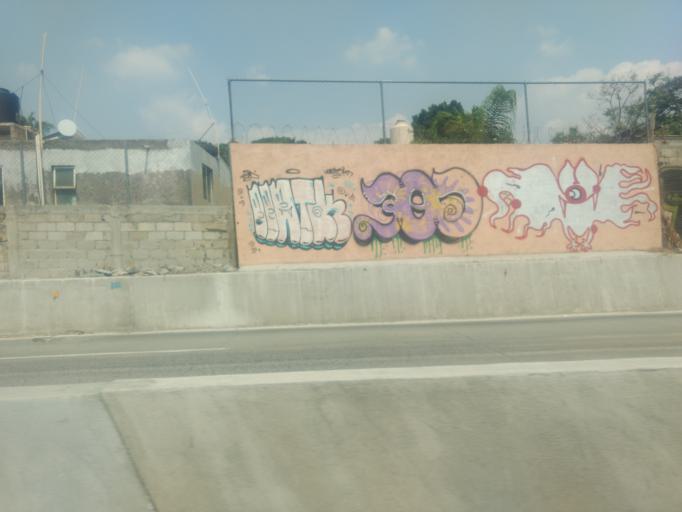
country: MX
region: Morelos
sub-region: Tepoztlan
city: Loma Bonita
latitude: 18.9284
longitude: -99.2020
